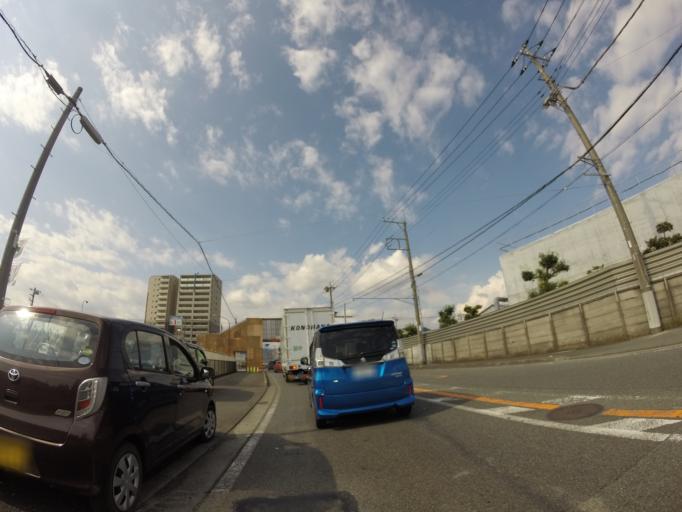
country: JP
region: Shizuoka
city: Fujinomiya
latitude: 35.2209
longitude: 138.6194
